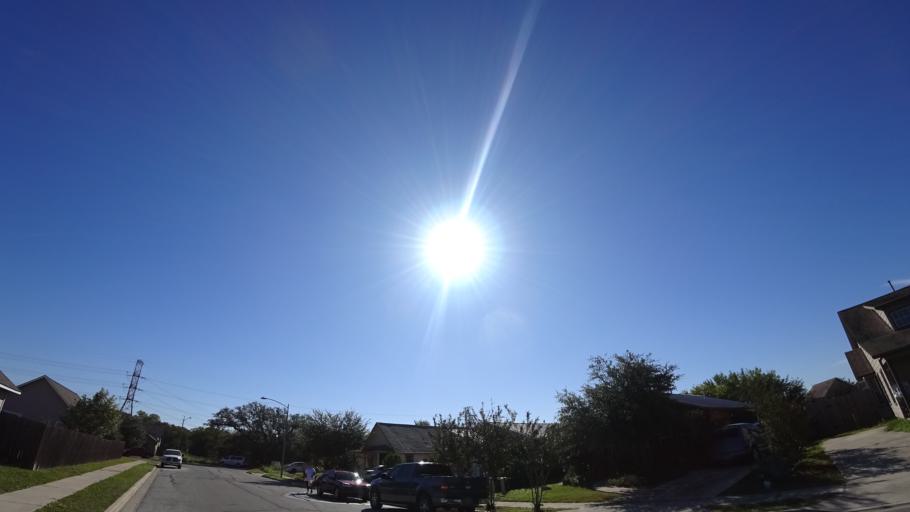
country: US
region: Texas
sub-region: Travis County
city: Austin
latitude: 30.2298
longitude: -97.6913
